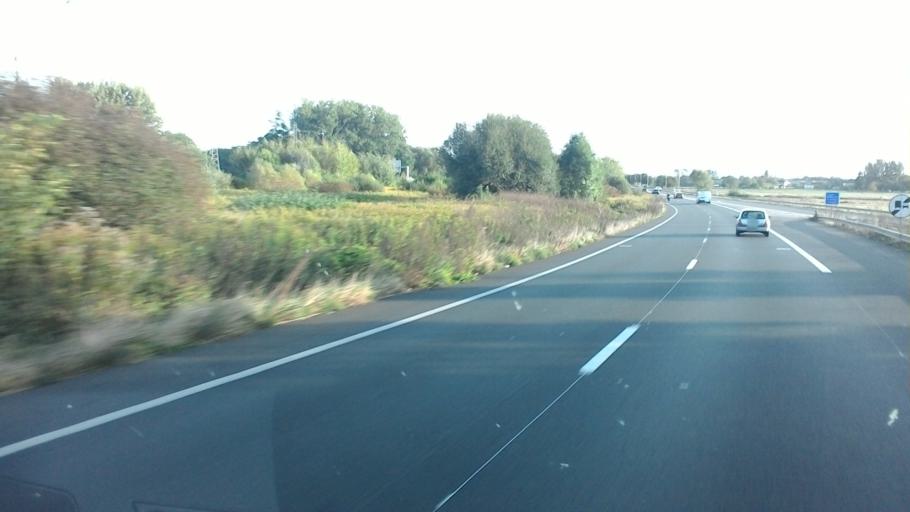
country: FR
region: Lorraine
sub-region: Departement de la Moselle
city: Richemont
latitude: 49.2877
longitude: 6.1721
